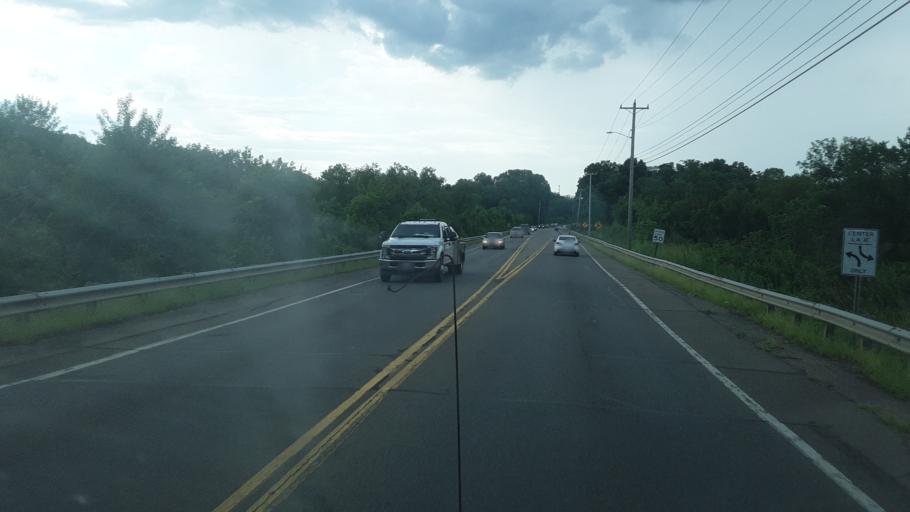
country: US
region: Tennessee
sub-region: Montgomery County
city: Clarksville
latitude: 36.5276
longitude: -87.2802
